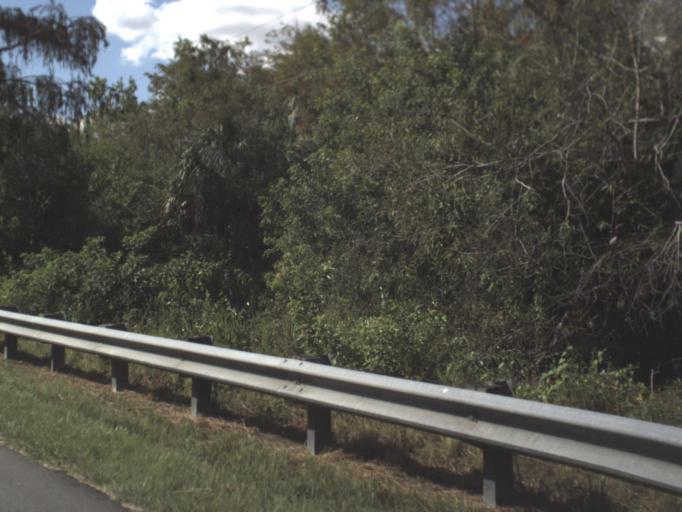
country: US
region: Florida
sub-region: Miami-Dade County
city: Kendall West
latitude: 25.8606
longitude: -81.0702
